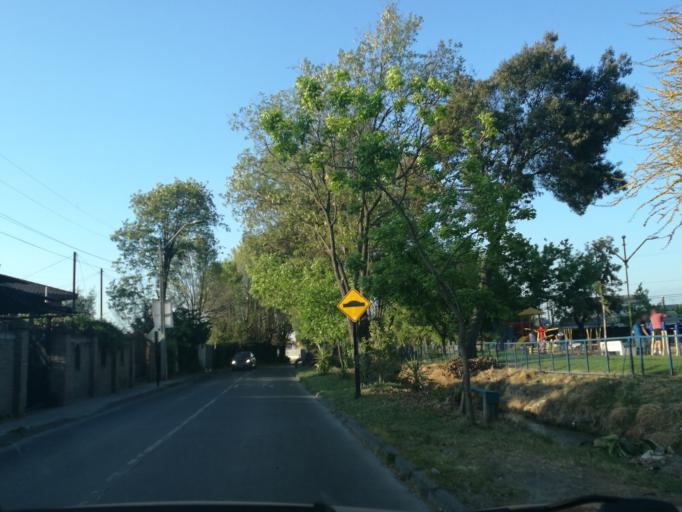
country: CL
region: O'Higgins
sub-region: Provincia de Cachapoal
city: Rancagua
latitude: -34.1893
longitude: -70.7294
